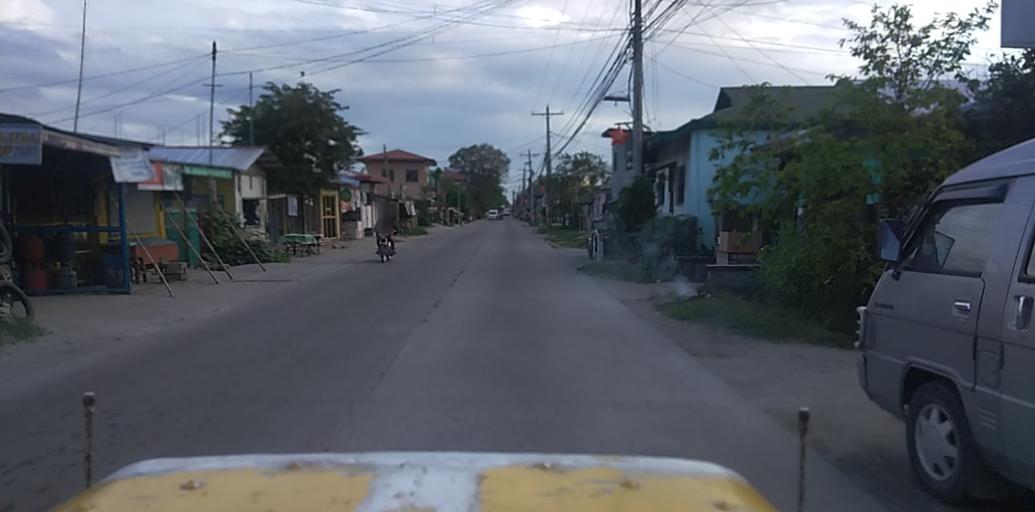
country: PH
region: Central Luzon
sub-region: Province of Pampanga
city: San Antonio
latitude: 15.1545
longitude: 120.6878
